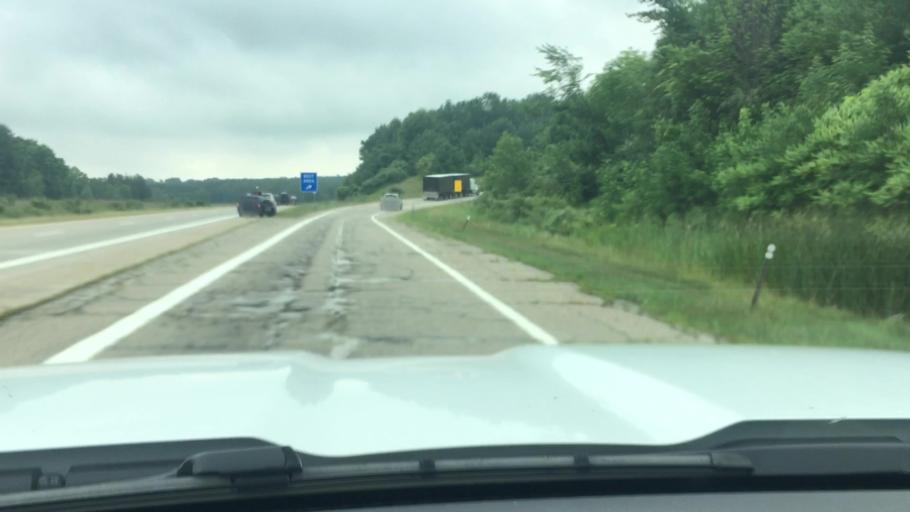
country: US
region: Michigan
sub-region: Lapeer County
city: Lapeer
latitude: 43.0083
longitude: -83.2232
